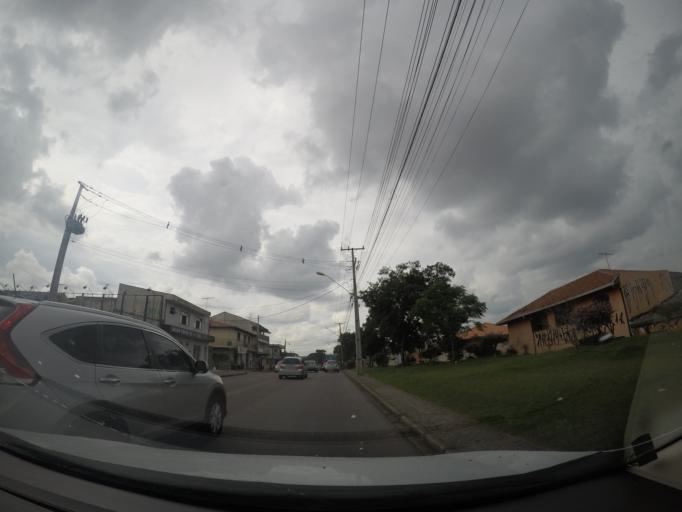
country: BR
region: Parana
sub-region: Sao Jose Dos Pinhais
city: Sao Jose dos Pinhais
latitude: -25.5234
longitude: -49.2433
